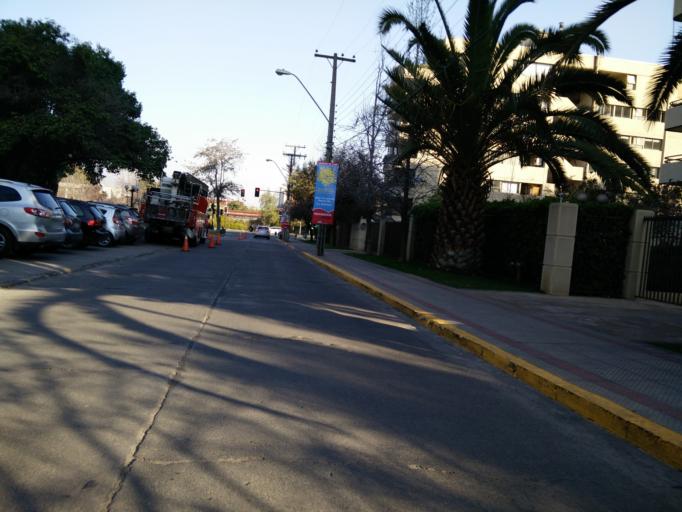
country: CL
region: Santiago Metropolitan
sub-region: Provincia de Santiago
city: Villa Presidente Frei, Nunoa, Santiago, Chile
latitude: -33.4322
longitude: -70.5954
